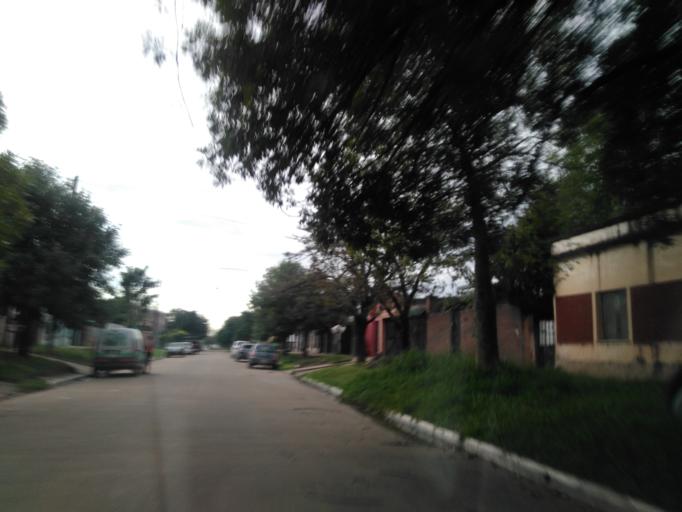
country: AR
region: Chaco
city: Resistencia
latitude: -27.4438
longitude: -58.9731
